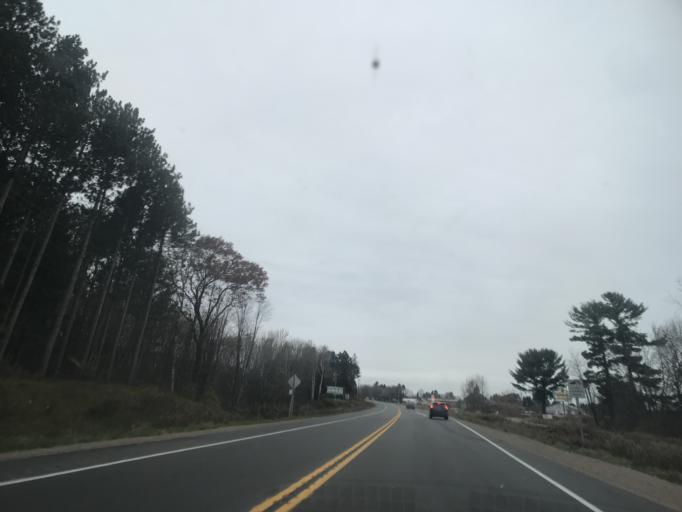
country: US
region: Wisconsin
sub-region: Menominee County
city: Legend Lake
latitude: 45.2968
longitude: -88.5154
